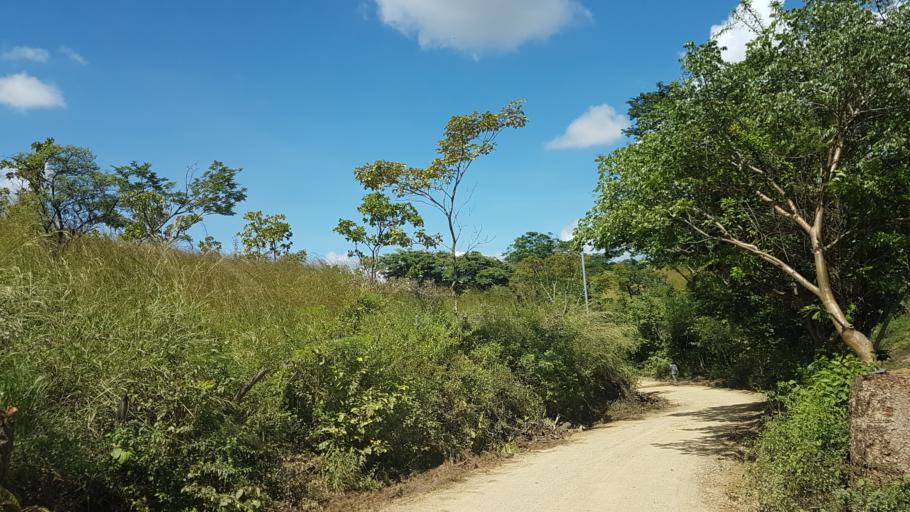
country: HN
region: El Paraiso
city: Oropoli
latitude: 13.7348
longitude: -86.6958
